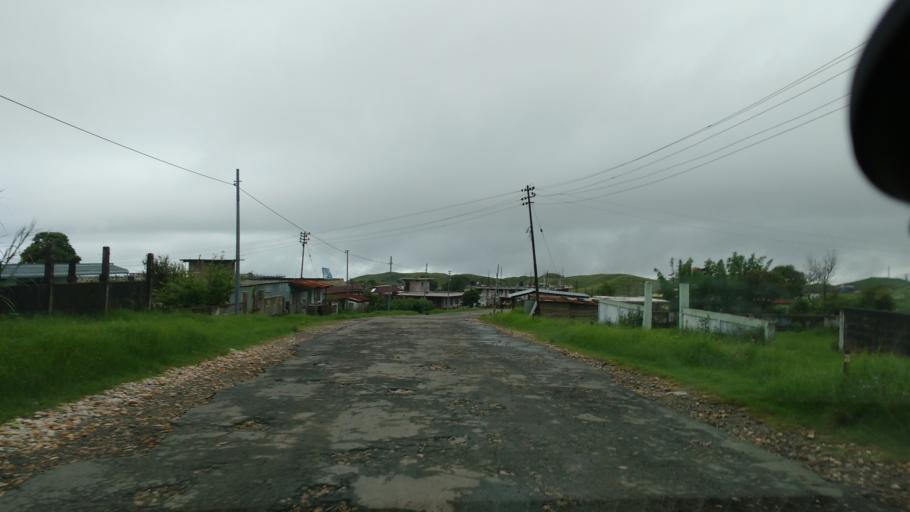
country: IN
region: Meghalaya
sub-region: East Khasi Hills
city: Cherrapunji
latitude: 25.2643
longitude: 91.7338
